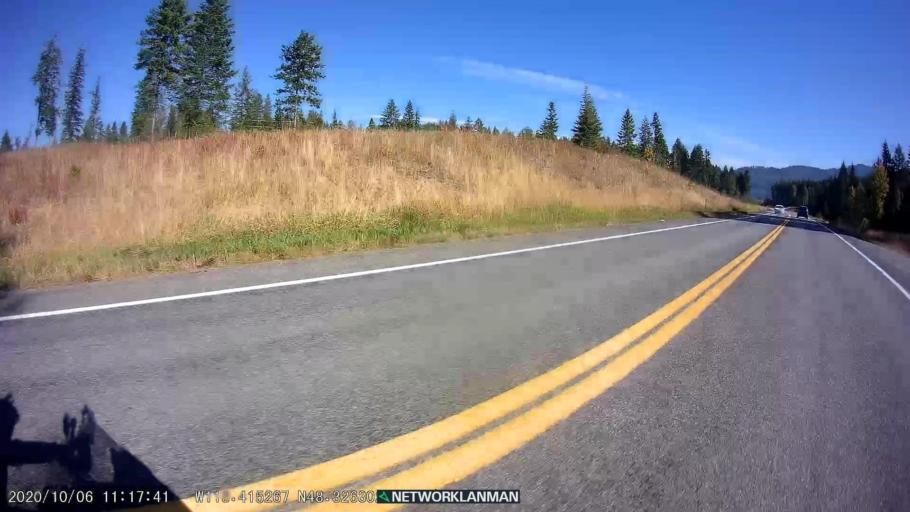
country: US
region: Idaho
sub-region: Bonner County
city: Ponderay
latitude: 48.3263
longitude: -116.4148
